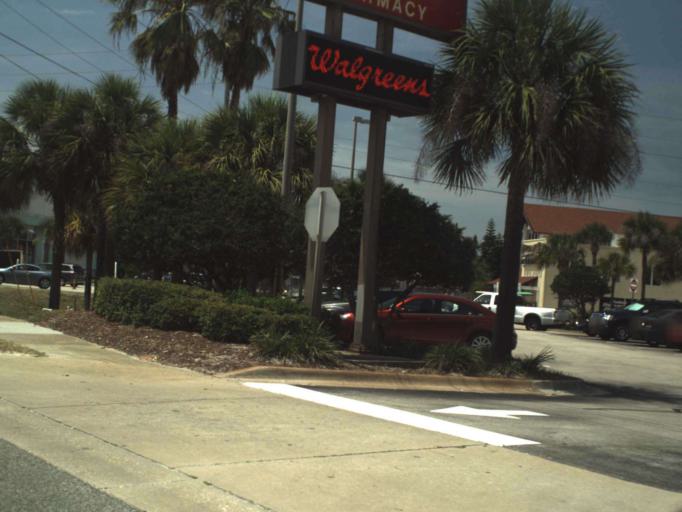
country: US
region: Florida
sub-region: Volusia County
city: New Smyrna Beach
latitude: 29.0285
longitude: -80.8924
